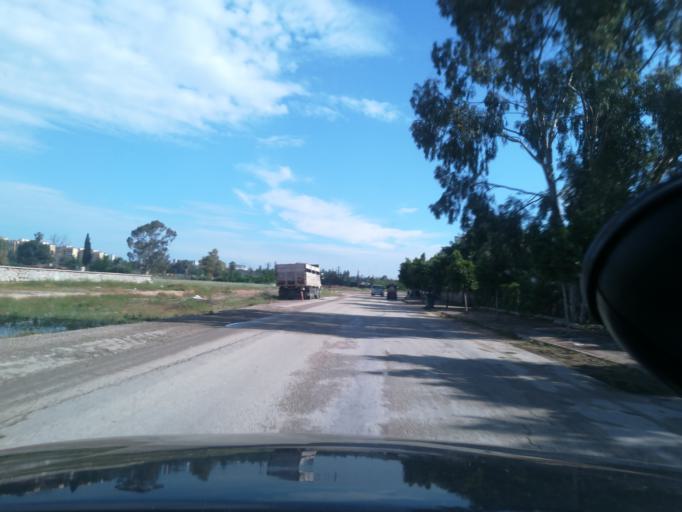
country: TR
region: Adana
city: Adana
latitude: 37.0197
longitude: 35.3627
